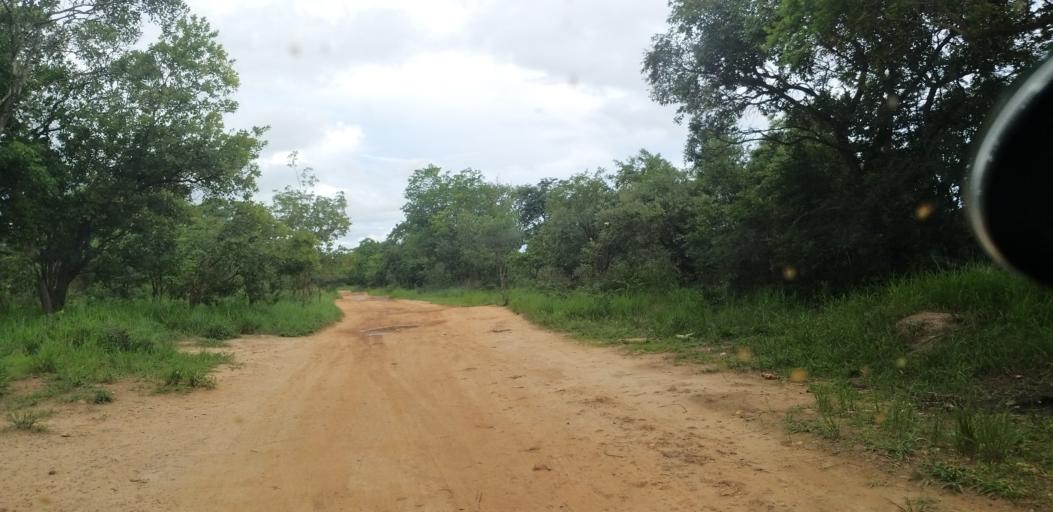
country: ZM
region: Lusaka
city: Lusaka
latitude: -15.1925
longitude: 28.4447
